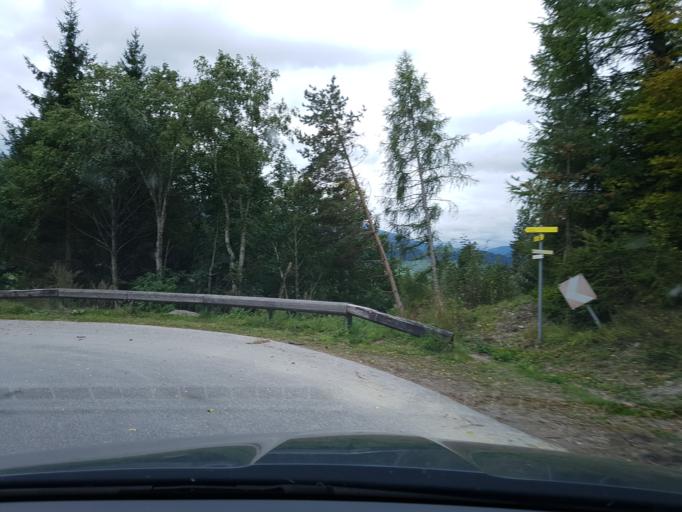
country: AT
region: Salzburg
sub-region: Politischer Bezirk Sankt Johann im Pongau
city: Radstadt
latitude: 47.3911
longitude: 13.4749
